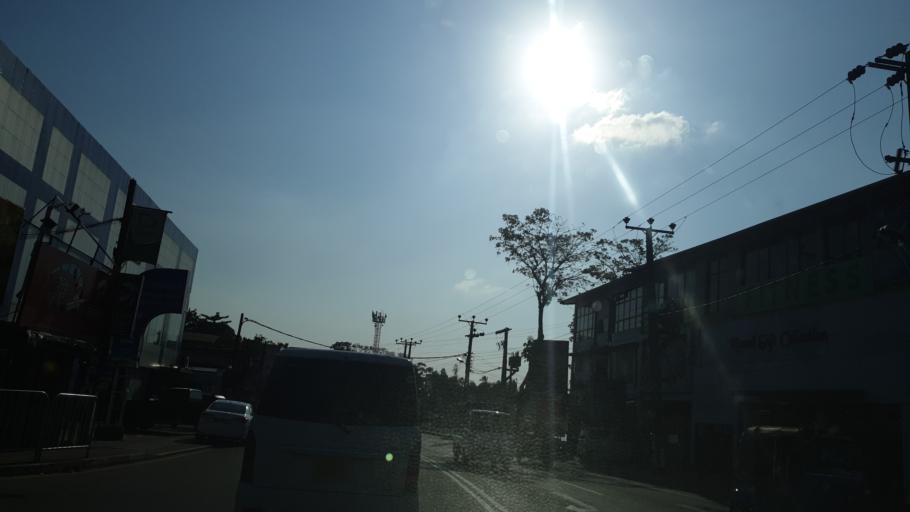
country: LK
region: Western
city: Battaramulla South
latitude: 6.8763
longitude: 79.9353
